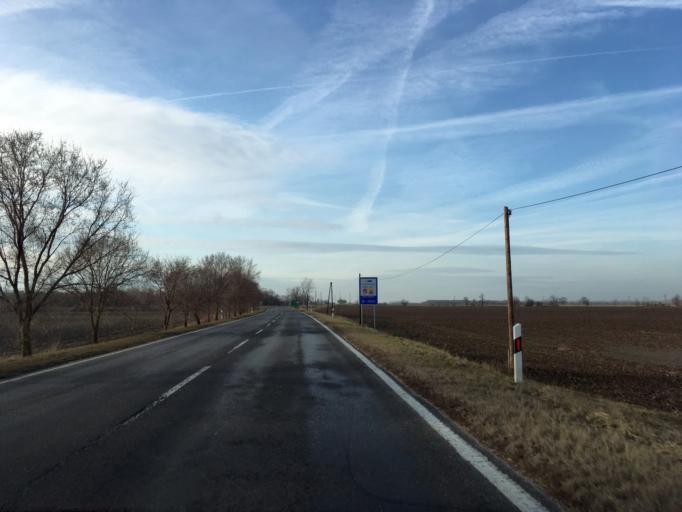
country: HU
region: Gyor-Moson-Sopron
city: Mosonszentmiklos
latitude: 47.7614
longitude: 17.4386
